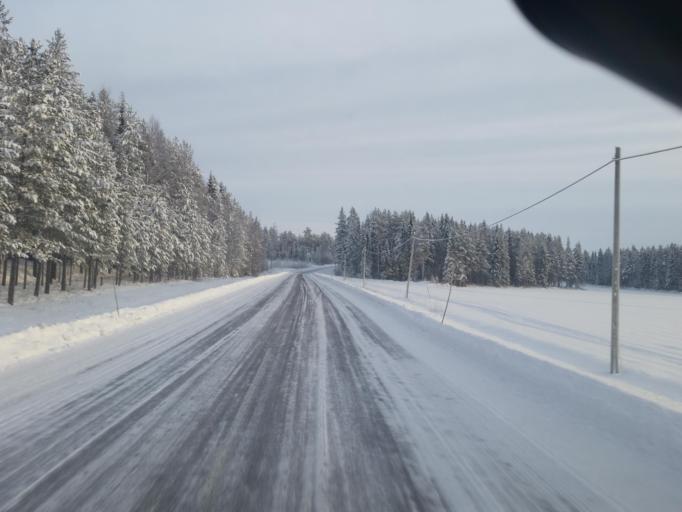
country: SE
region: Norrbotten
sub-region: Pitea Kommun
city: Norrfjarden
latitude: 65.5143
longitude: 21.5201
